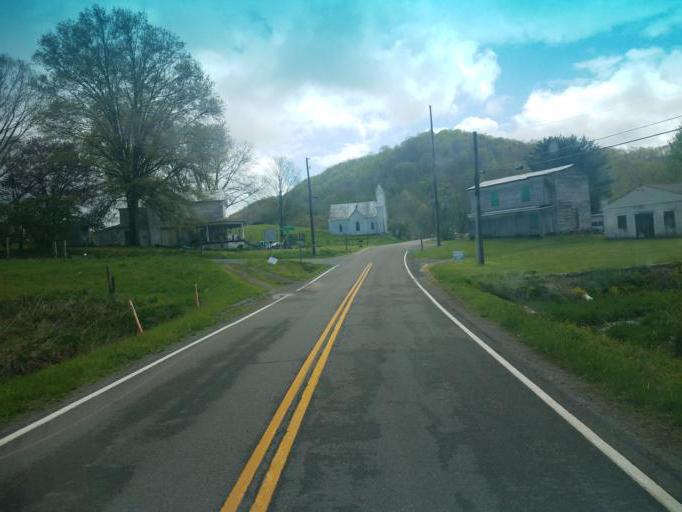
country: US
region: Virginia
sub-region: Wythe County
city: Rural Retreat
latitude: 37.0180
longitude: -81.3440
